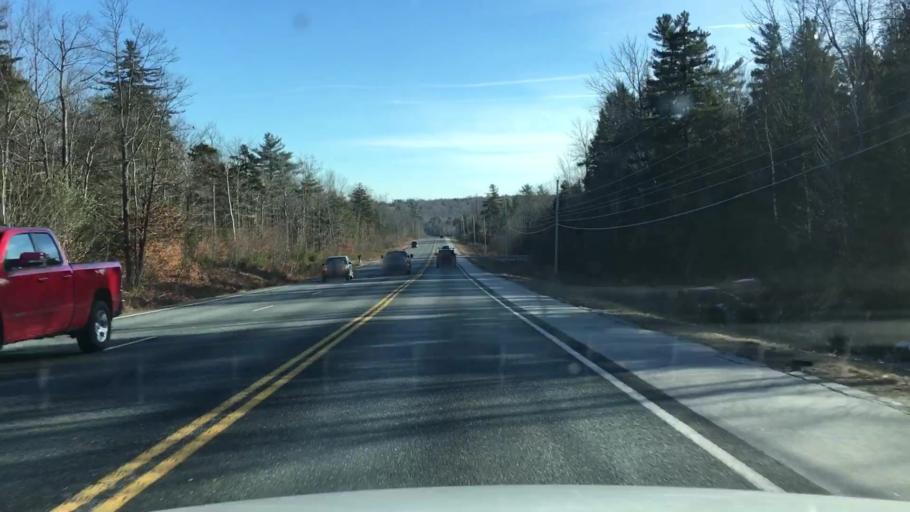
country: US
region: Maine
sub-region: Hancock County
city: Dedham
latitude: 44.6406
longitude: -68.5518
